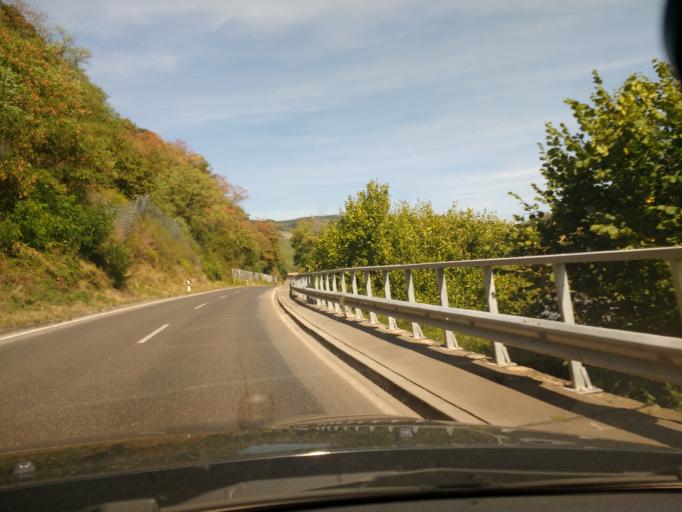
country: DE
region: Rheinland-Pfalz
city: Ayl
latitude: 49.6218
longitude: 6.5641
